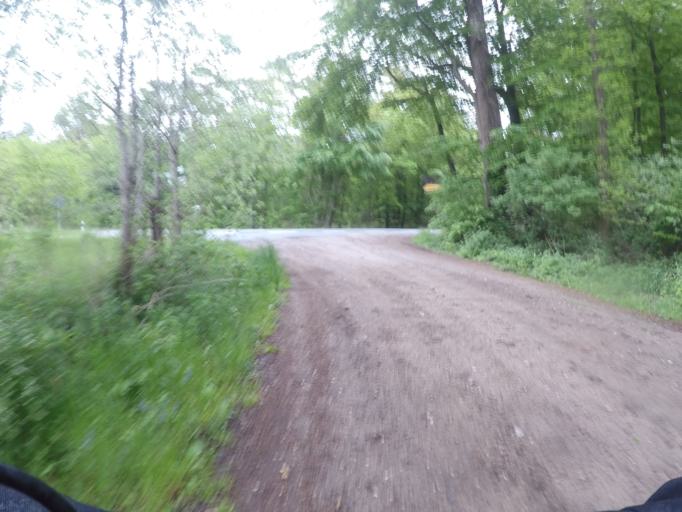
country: DE
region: Schleswig-Holstein
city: Heidmuhlen
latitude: 53.9626
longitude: 10.1219
